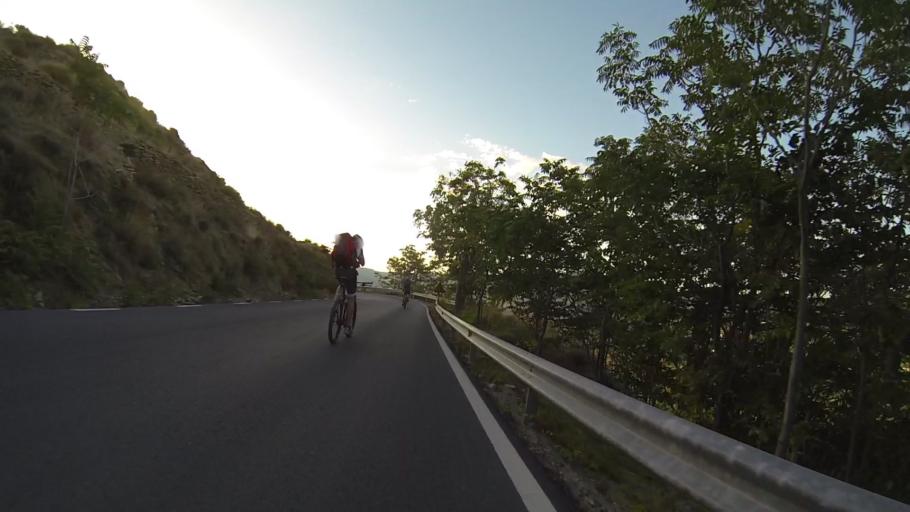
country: ES
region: Andalusia
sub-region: Provincia de Granada
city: Berchules
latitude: 36.9834
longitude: -3.1486
